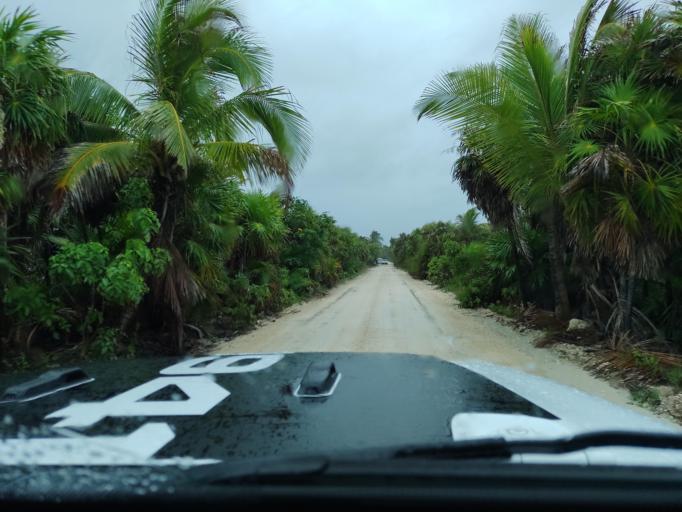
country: MX
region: Quintana Roo
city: Tulum
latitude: 19.9852
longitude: -87.4654
